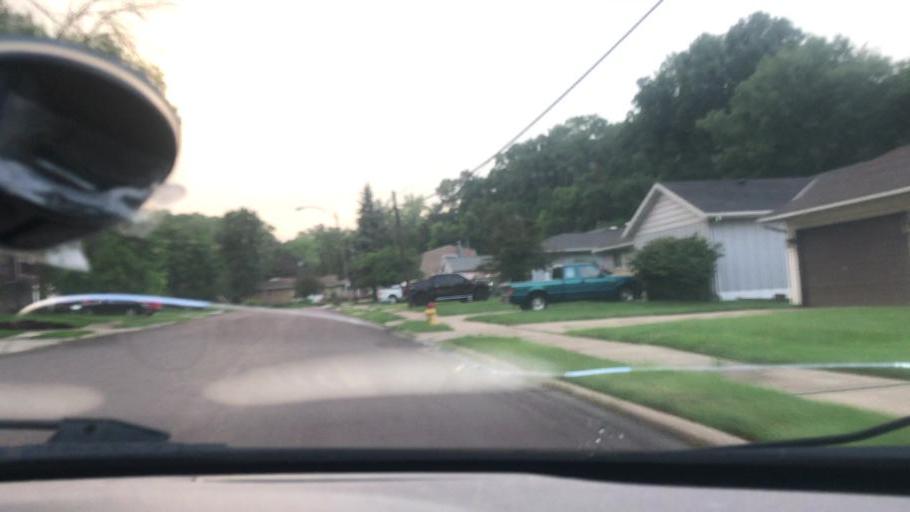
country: US
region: Illinois
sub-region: Tazewell County
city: Pekin
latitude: 40.5568
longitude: -89.6163
